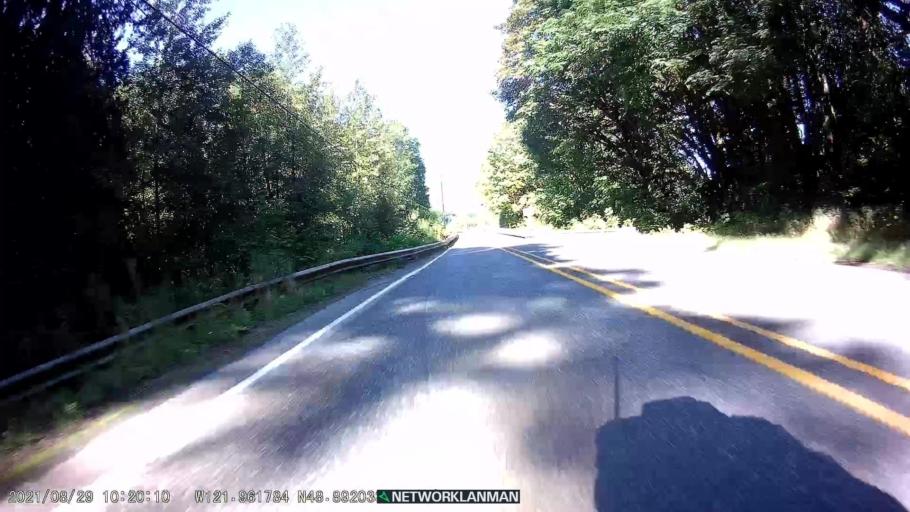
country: US
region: Washington
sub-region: Whatcom County
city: Peaceful Valley
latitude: 48.8910
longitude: -121.9615
